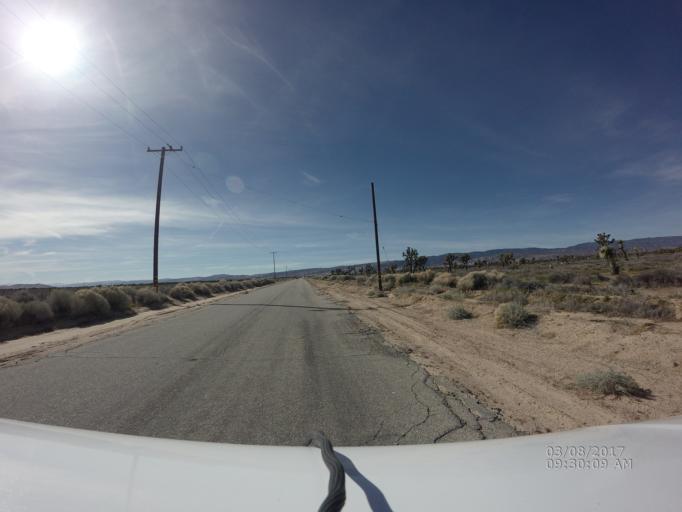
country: US
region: California
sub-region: Los Angeles County
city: Green Valley
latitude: 34.7945
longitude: -118.4668
